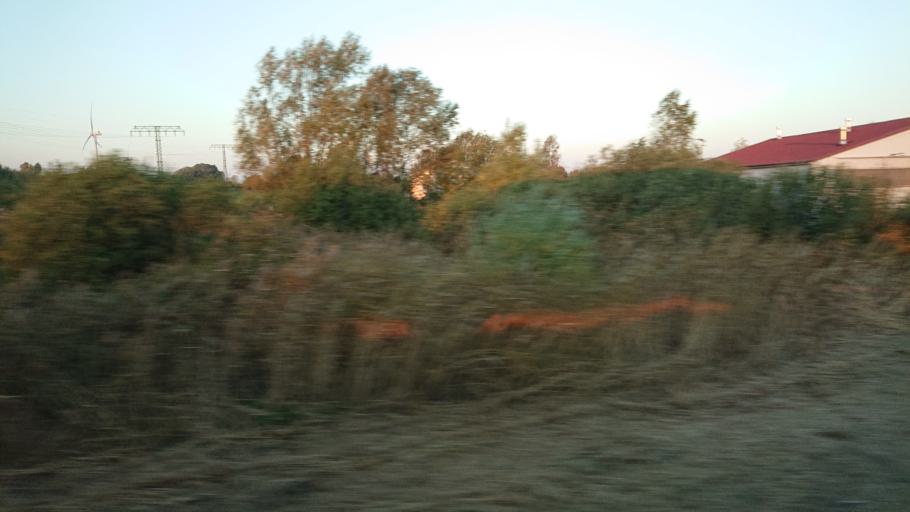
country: DE
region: Mecklenburg-Vorpommern
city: Greifswald
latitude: 54.0650
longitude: 13.3795
